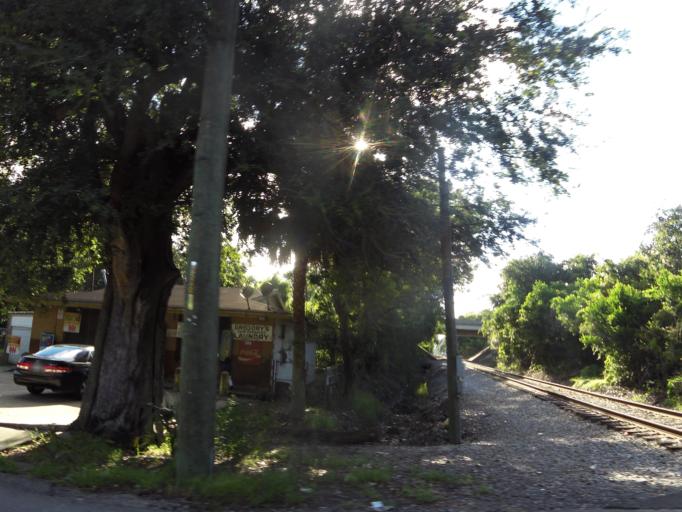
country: US
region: Florida
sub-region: Duval County
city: Jacksonville
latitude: 30.3533
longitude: -81.6671
